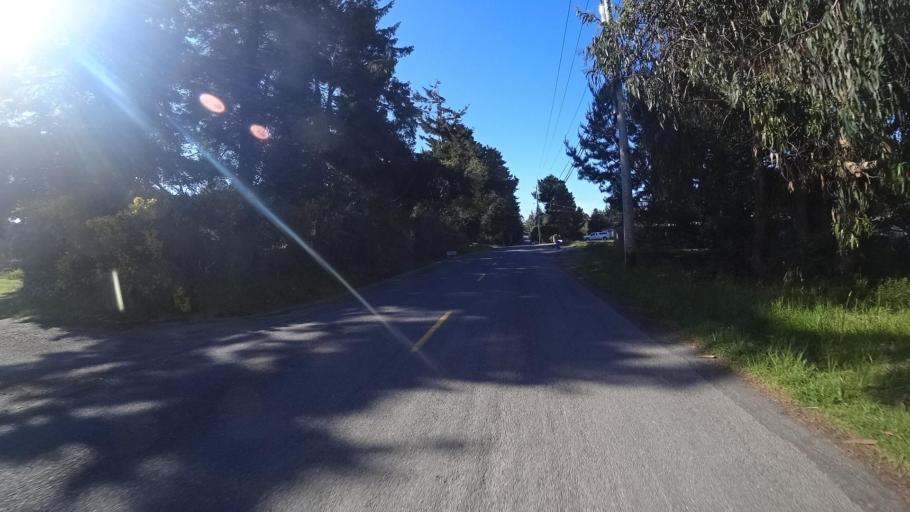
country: US
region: California
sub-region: Humboldt County
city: McKinleyville
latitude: 40.9701
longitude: -124.0959
